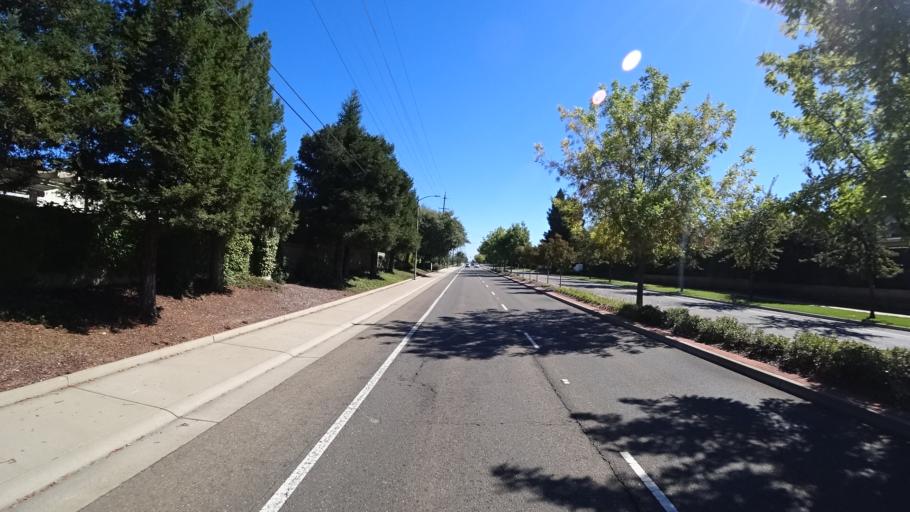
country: US
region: California
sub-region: Sacramento County
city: Elk Grove
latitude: 38.4236
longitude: -121.3631
